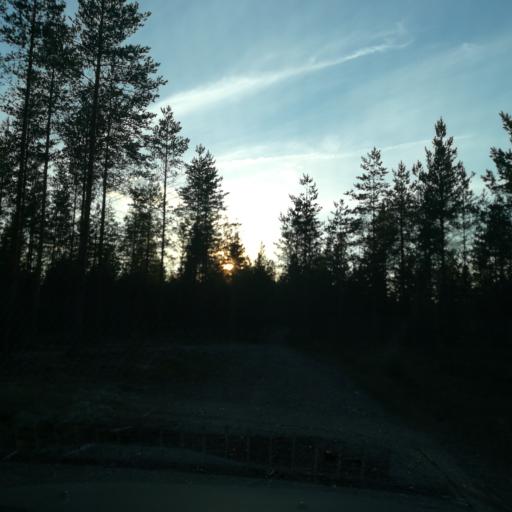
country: FI
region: Southern Savonia
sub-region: Mikkeli
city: Puumala
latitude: 61.4332
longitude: 28.4645
